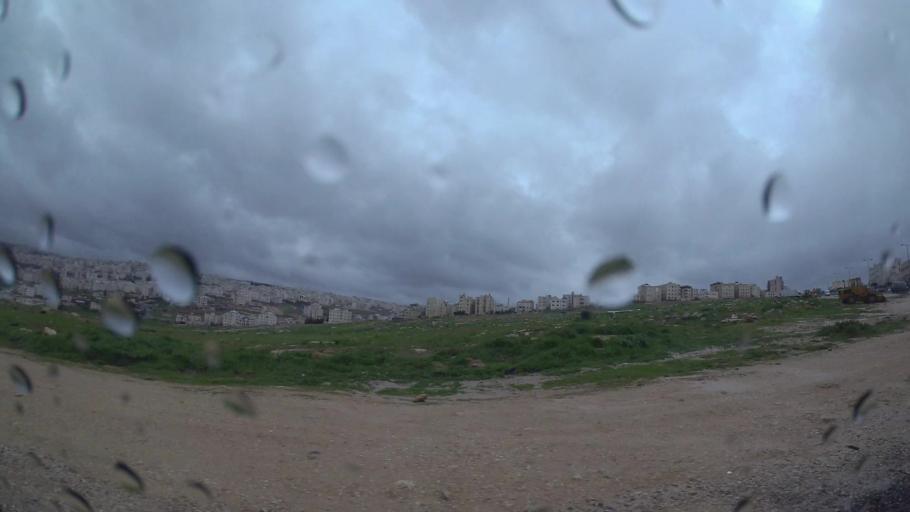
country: JO
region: Amman
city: Al Jubayhah
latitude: 32.0438
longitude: 35.8988
